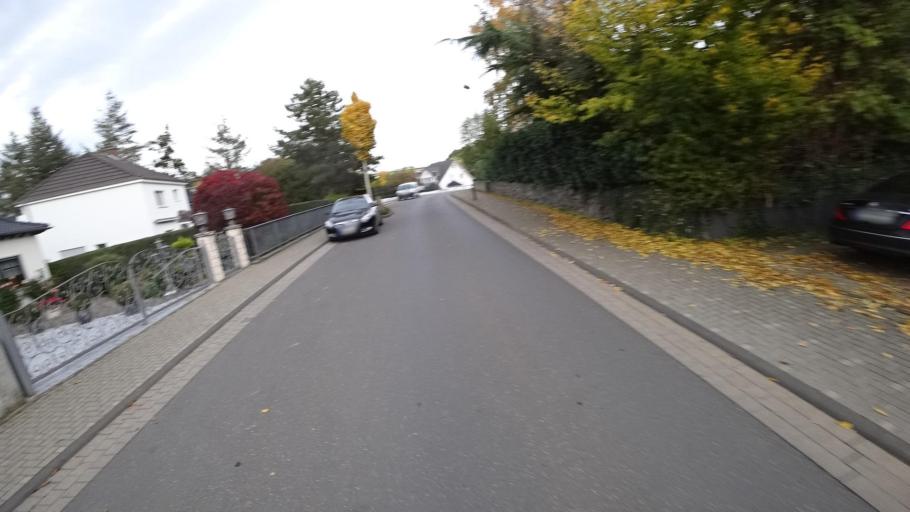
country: DE
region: Rheinland-Pfalz
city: Schalkenbach
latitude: 50.5413
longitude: 7.1572
